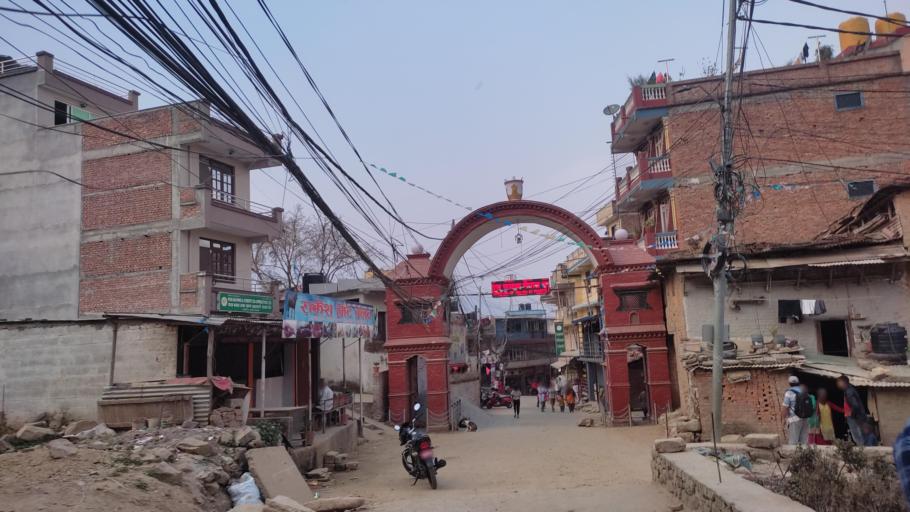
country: NP
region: Central Region
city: Kirtipur
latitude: 27.6695
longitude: 85.2496
